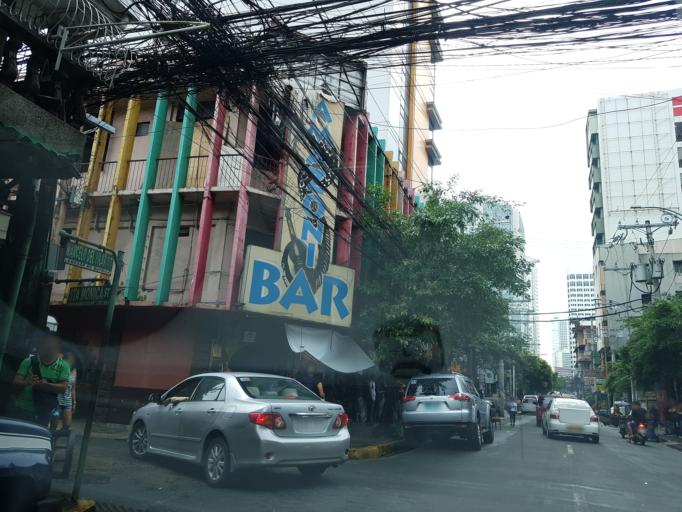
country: PH
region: Metro Manila
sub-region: City of Manila
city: Port Area
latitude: 14.5758
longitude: 120.9811
